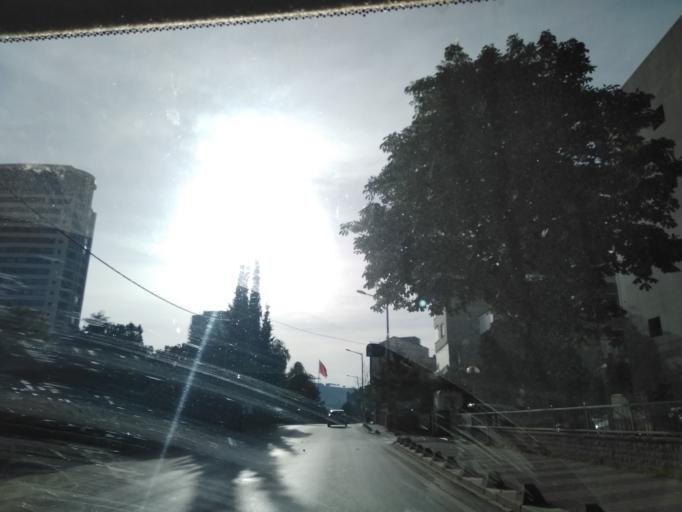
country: TR
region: Istanbul
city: Maltepe
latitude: 40.9174
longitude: 29.1584
